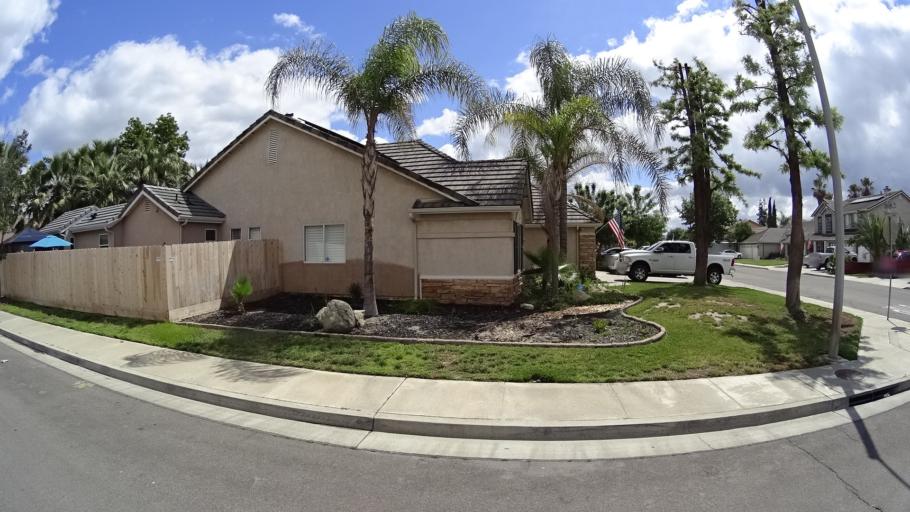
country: US
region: California
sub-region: Kings County
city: Lucerne
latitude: 36.3627
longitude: -119.6566
